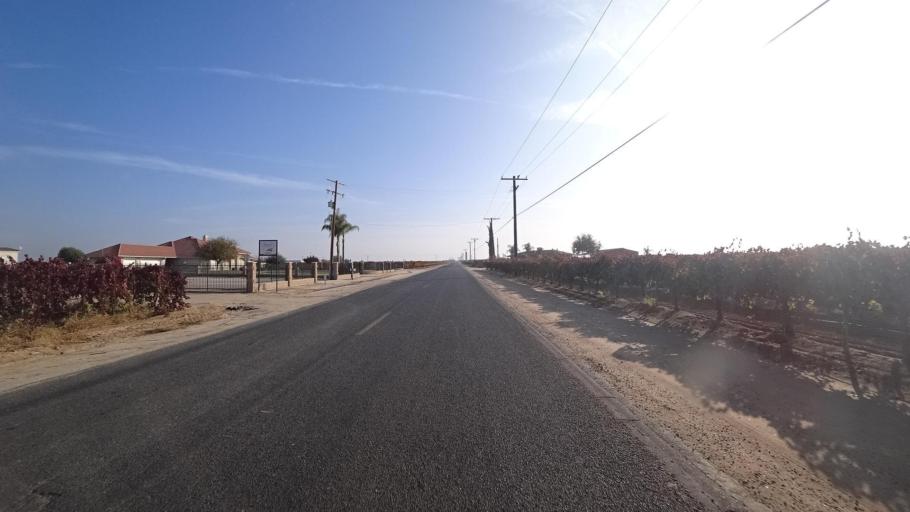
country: US
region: California
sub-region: Kern County
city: McFarland
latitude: 35.6746
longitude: -119.1927
